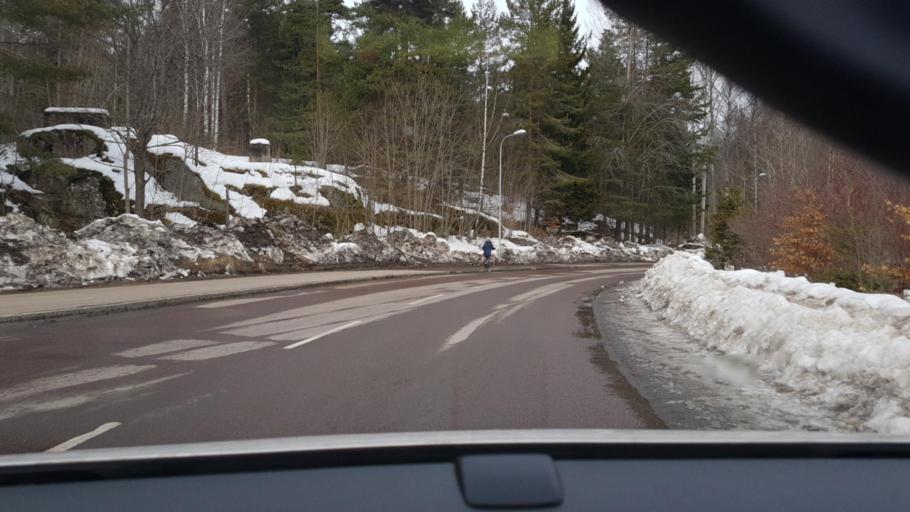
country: SE
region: Vaermland
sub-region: Eda Kommun
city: Amotfors
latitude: 59.7577
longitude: 12.3573
